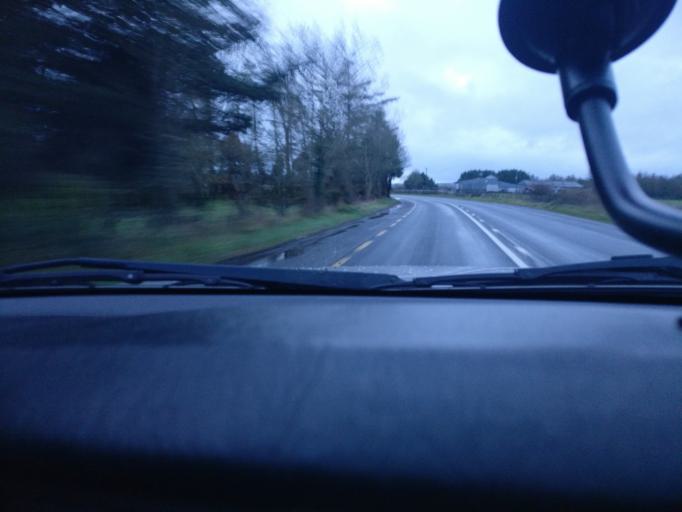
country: IE
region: Connaught
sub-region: County Galway
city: Loughrea
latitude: 53.2429
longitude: -8.4499
